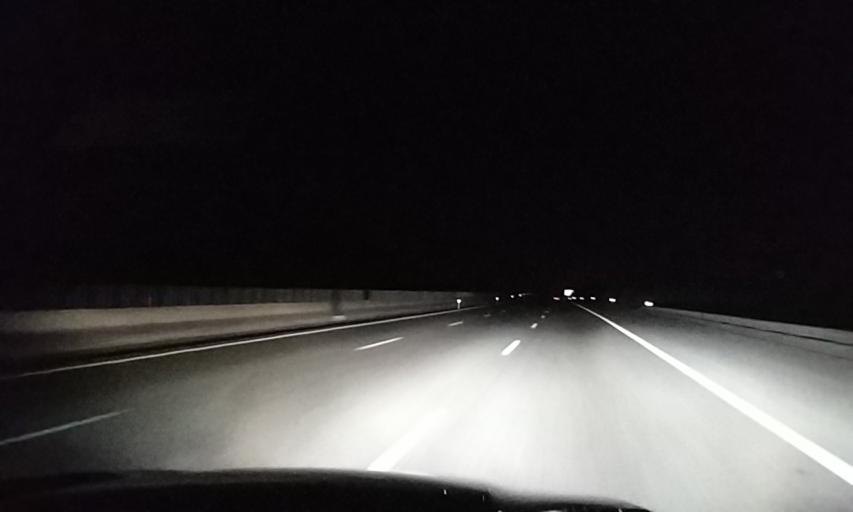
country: PT
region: Santarem
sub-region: Alcanena
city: Alcanena
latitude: 39.3840
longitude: -8.6331
